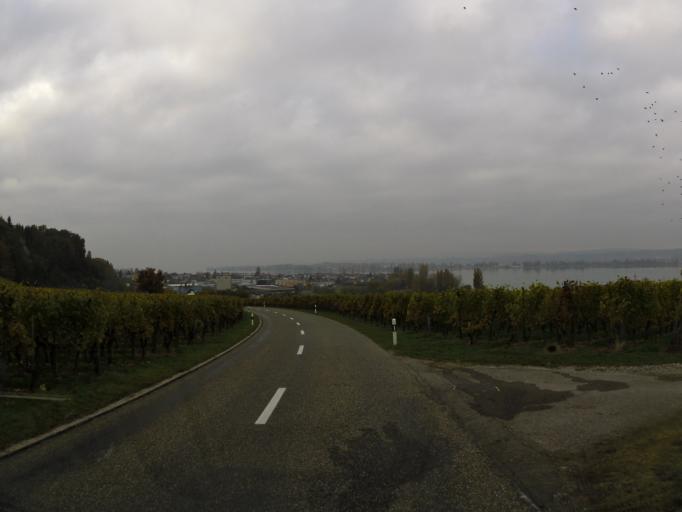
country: CH
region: Thurgau
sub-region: Kreuzlingen District
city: Ermatingen
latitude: 47.6626
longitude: 9.0964
